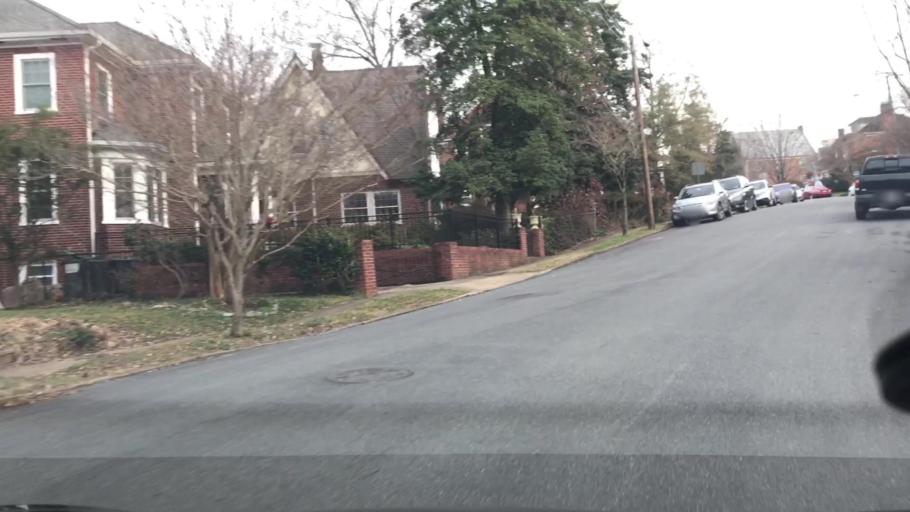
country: US
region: Virginia
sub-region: City of Charlottesville
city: Charlottesville
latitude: 38.0351
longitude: -78.4777
